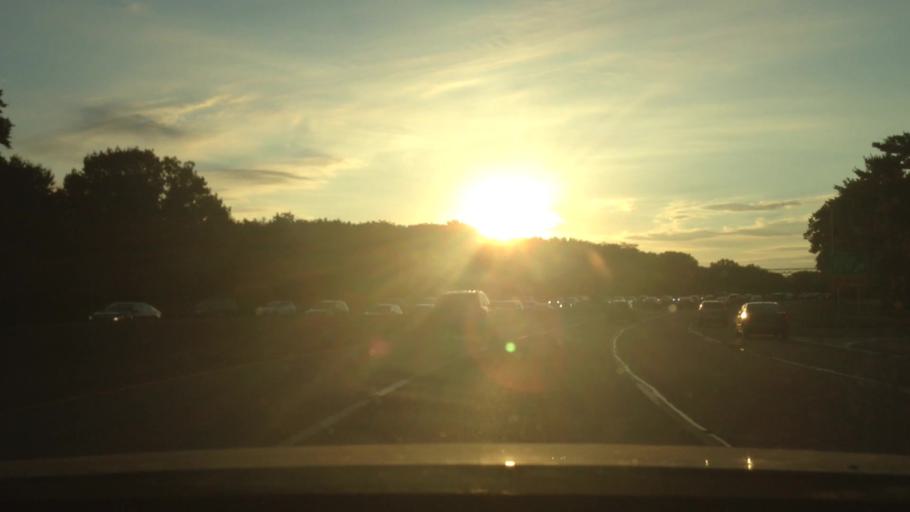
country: US
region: New York
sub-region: Nassau County
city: North Valley Stream
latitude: 40.6867
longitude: -73.7150
